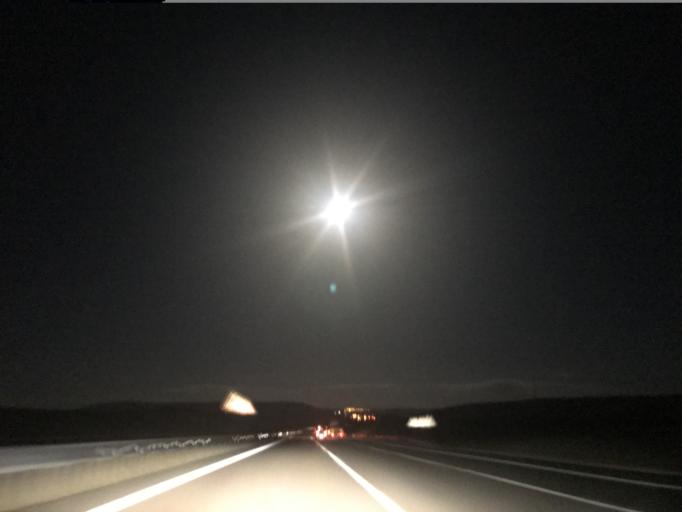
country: TR
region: Nigde
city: Ulukisla
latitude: 37.6353
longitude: 34.4289
